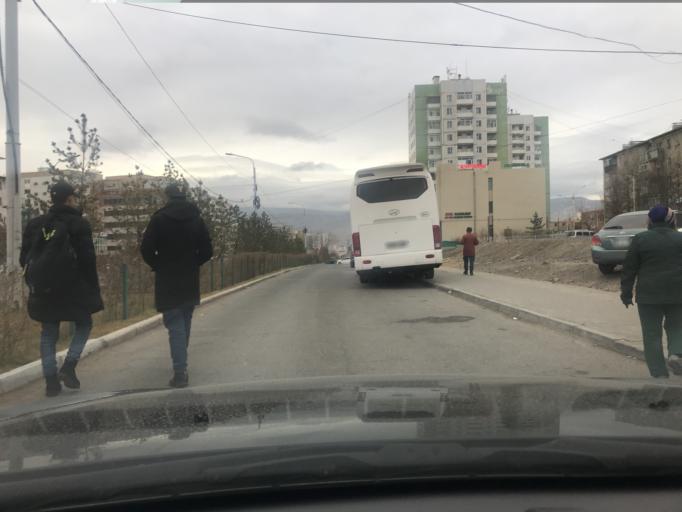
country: MN
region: Ulaanbaatar
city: Ulaanbaatar
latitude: 47.9260
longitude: 106.9411
